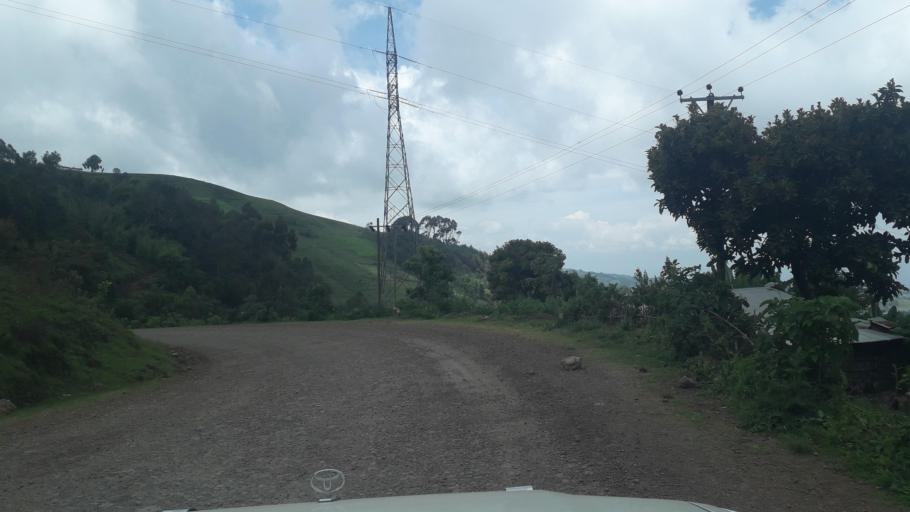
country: ET
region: Oromiya
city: Jima
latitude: 7.4473
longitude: 36.8784
